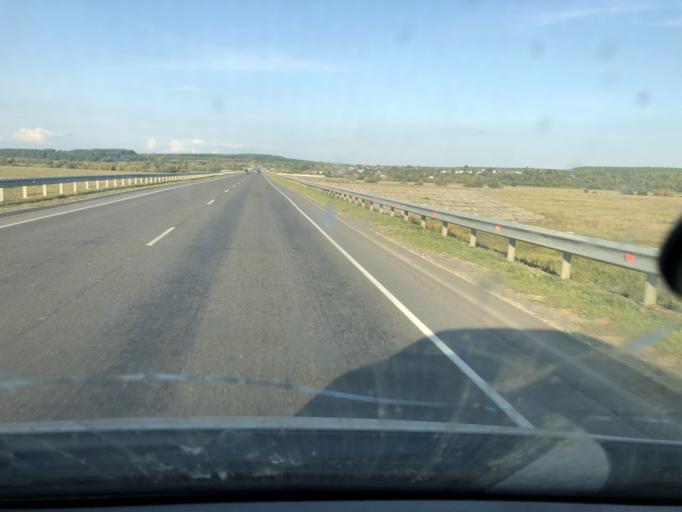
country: RU
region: Kaluga
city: Peremyshl'
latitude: 54.2856
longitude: 36.1601
